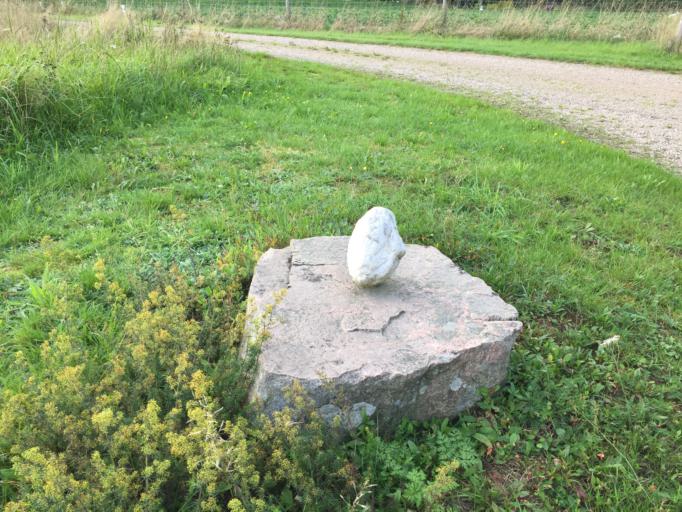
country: SE
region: Skane
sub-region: Perstorps Kommun
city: Perstorp
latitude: 56.2111
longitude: 13.3373
